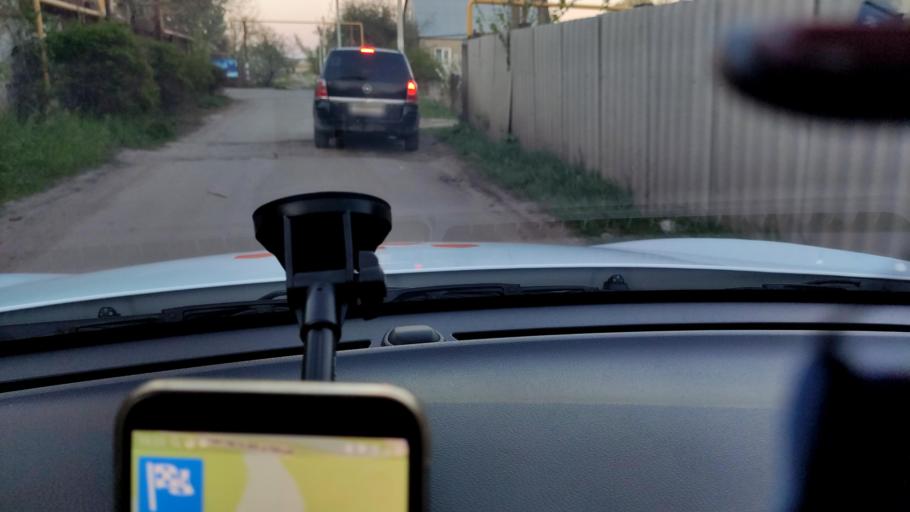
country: RU
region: Voronezj
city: Somovo
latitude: 51.6816
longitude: 39.3302
